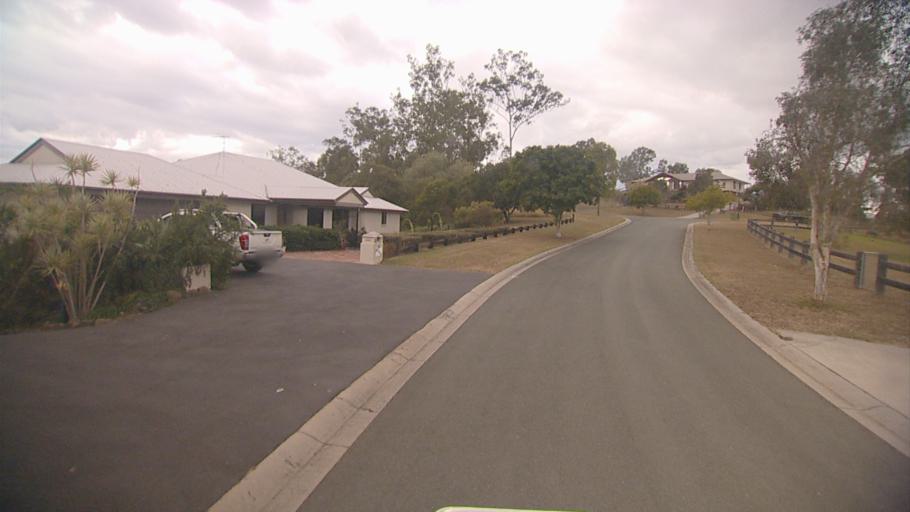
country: AU
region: Queensland
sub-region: Logan
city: Cedar Vale
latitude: -27.8680
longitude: 153.0727
